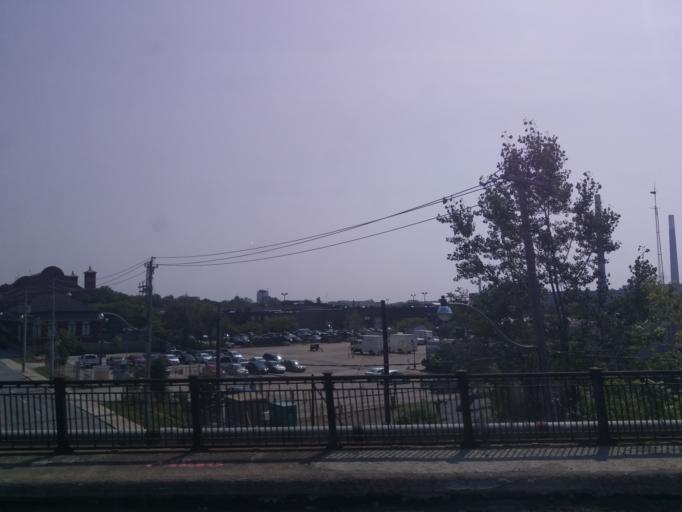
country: CA
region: Ontario
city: Toronto
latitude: 43.6568
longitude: -79.3464
